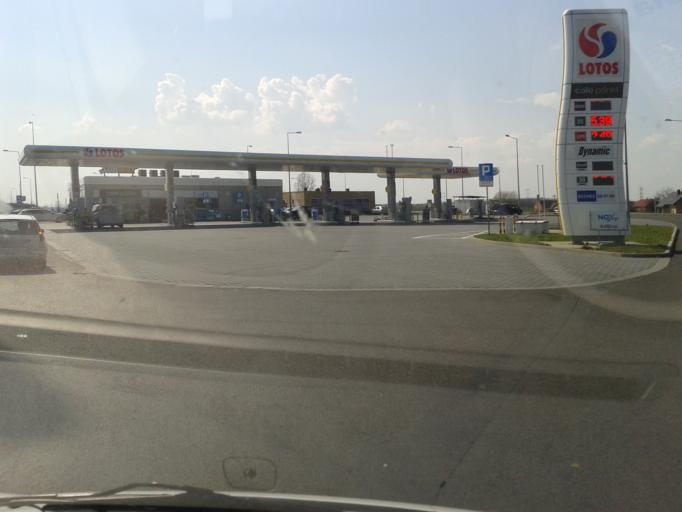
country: PL
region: Lesser Poland Voivodeship
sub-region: Powiat tarnowski
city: Wierzchoslawice
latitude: 50.0426
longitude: 20.8895
